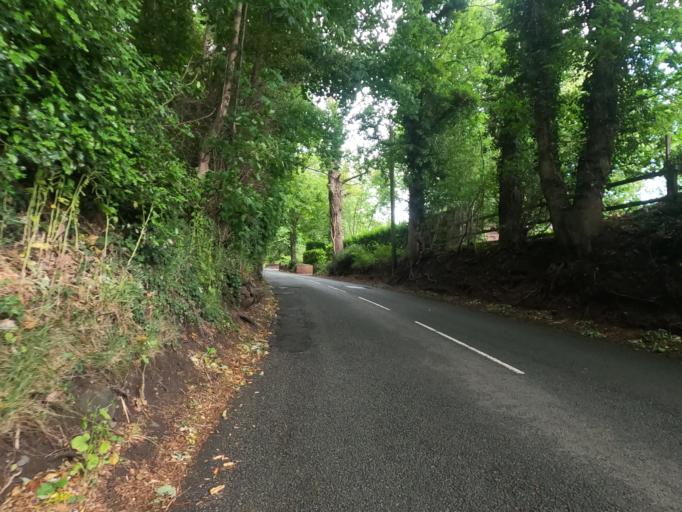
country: GB
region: England
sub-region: Cheshire West and Chester
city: Cuddington
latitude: 53.2415
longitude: -2.6088
